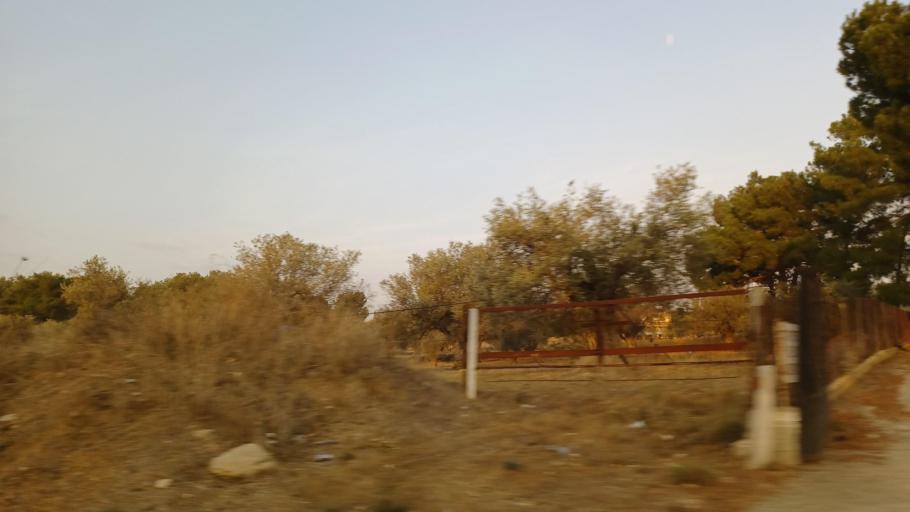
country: CY
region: Larnaka
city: Mosfiloti
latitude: 34.9491
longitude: 33.4178
